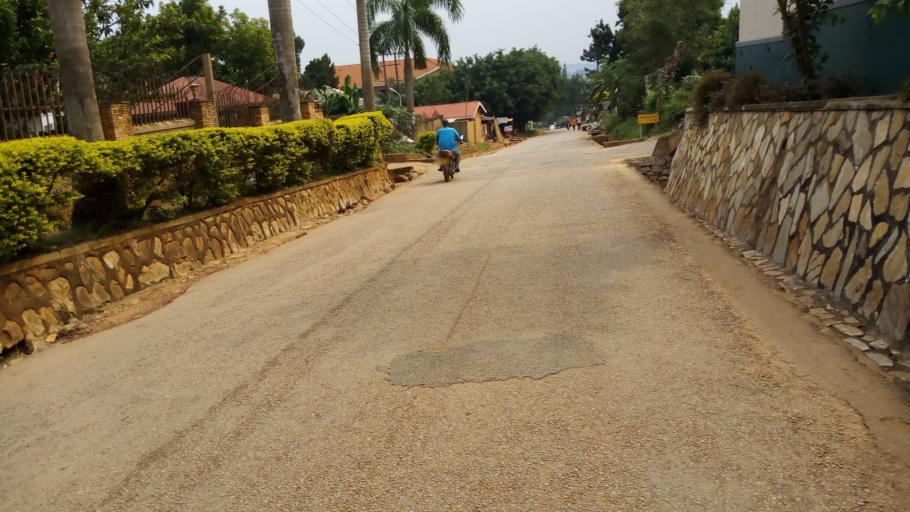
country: UG
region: Central Region
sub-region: Wakiso District
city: Kireka
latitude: 0.3096
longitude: 32.6429
